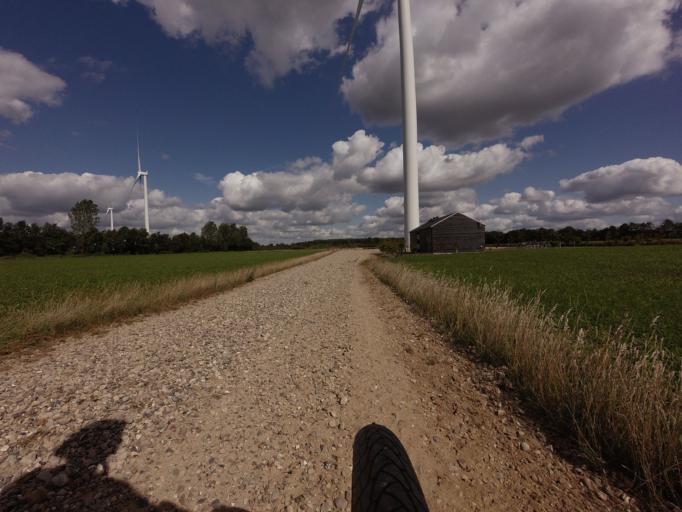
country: DK
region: Central Jutland
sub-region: Ikast-Brande Kommune
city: Brande
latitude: 55.9747
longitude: 9.1252
